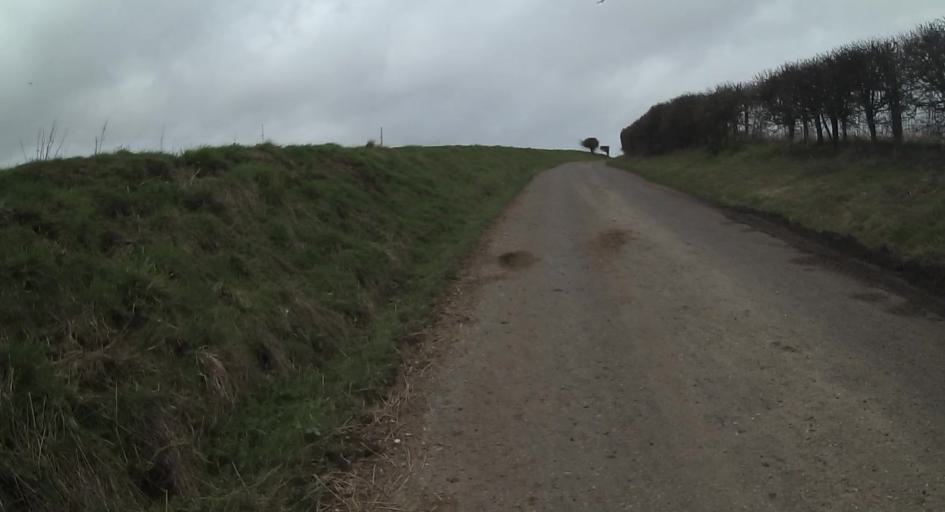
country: GB
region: England
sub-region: Hampshire
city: Kingsclere
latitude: 51.3067
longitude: -1.2178
